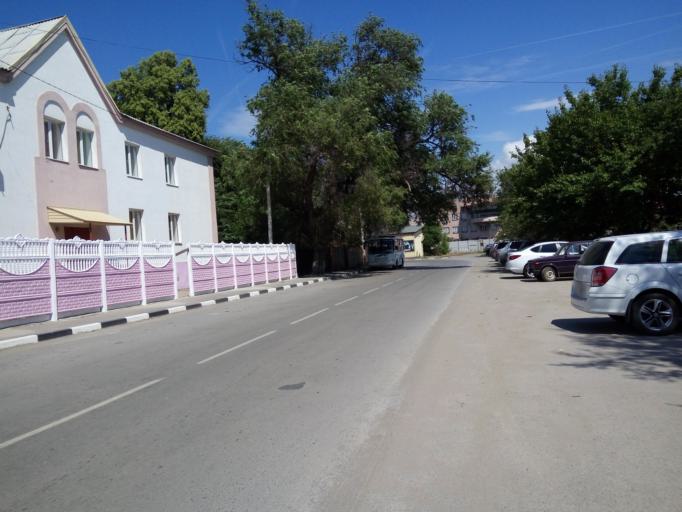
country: RU
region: Rostov
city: Bataysk
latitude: 47.1355
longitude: 39.7540
